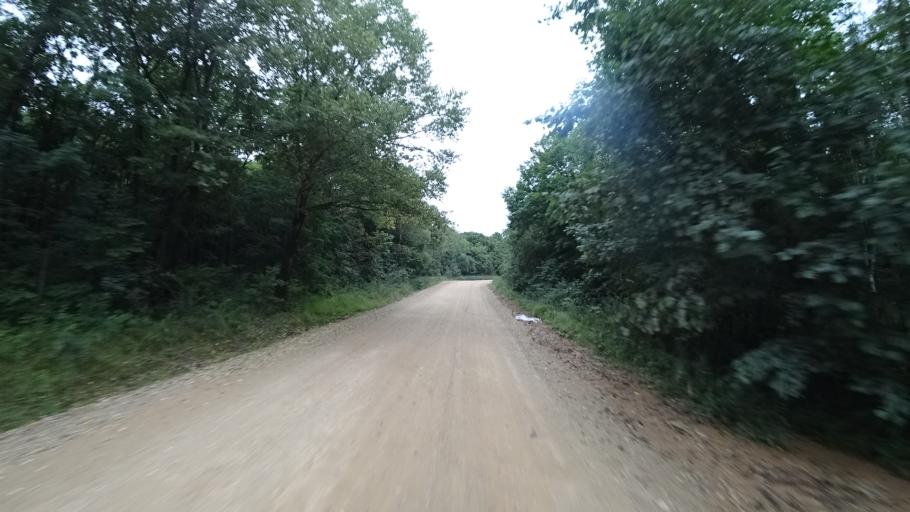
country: RU
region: Primorskiy
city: Rettikhovka
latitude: 44.1849
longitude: 132.8177
